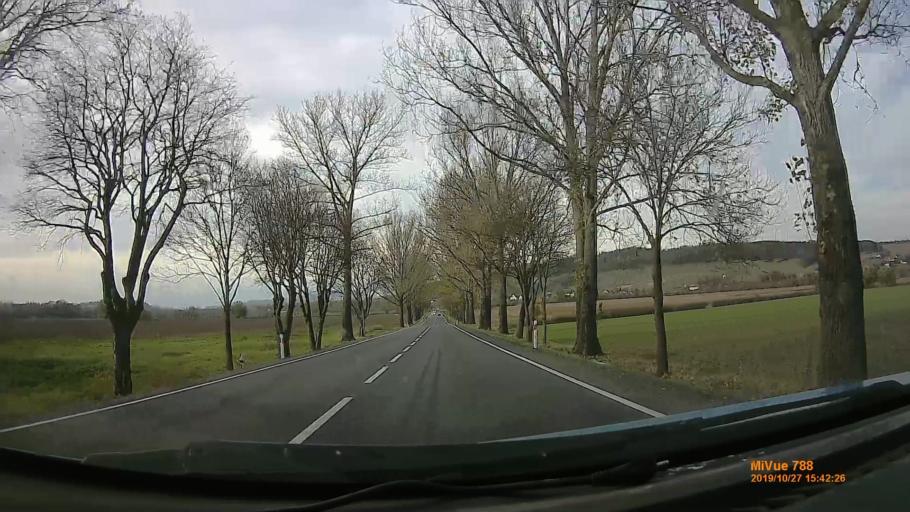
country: PL
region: Lower Silesian Voivodeship
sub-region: Powiat klodzki
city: Klodzko
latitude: 50.4588
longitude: 16.6277
